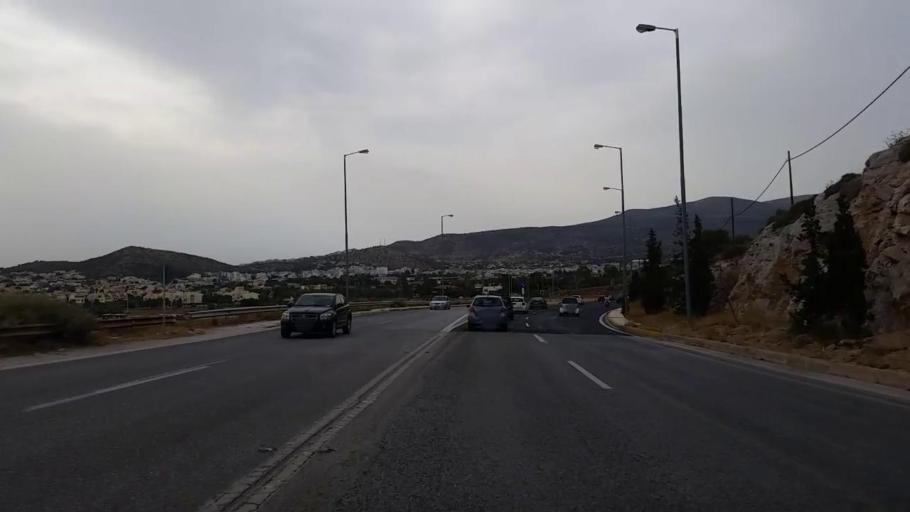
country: GR
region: Attica
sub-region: Nomarchia Anatolikis Attikis
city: Vari
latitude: 37.8198
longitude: 23.8178
